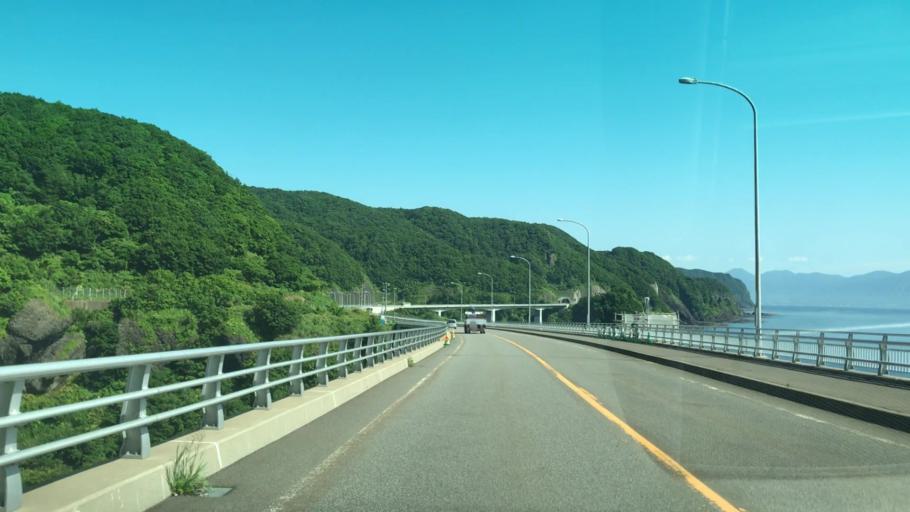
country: JP
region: Hokkaido
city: Iwanai
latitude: 43.1313
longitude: 140.4355
